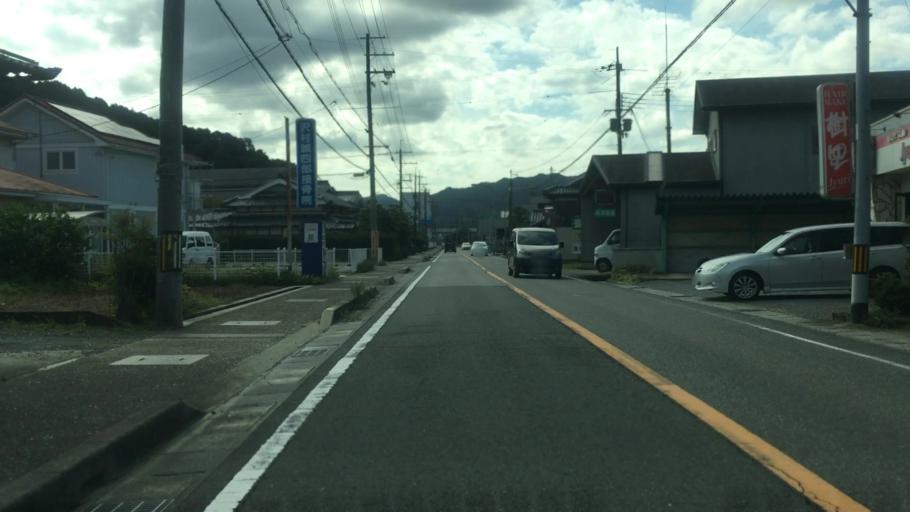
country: JP
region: Kyoto
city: Fukuchiyama
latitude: 35.1559
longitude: 135.0520
